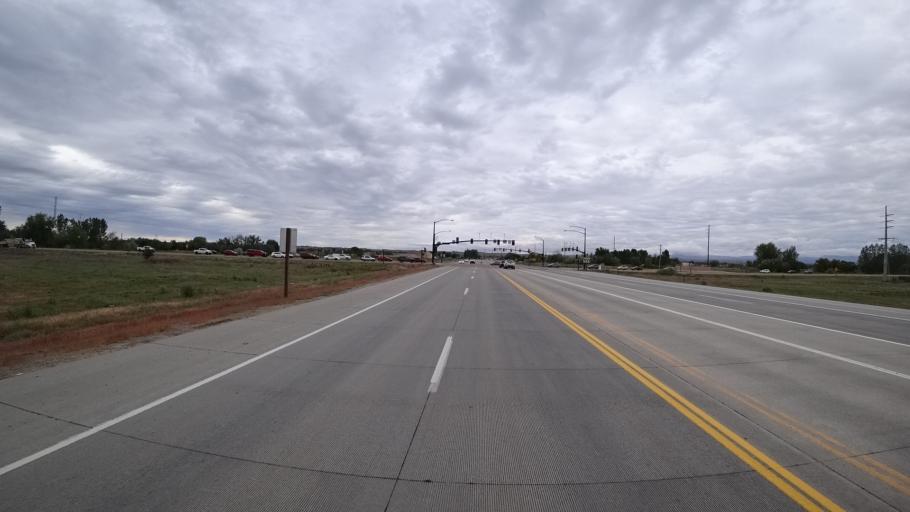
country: US
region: Idaho
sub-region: Ada County
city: Star
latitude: 43.6907
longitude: -116.4603
